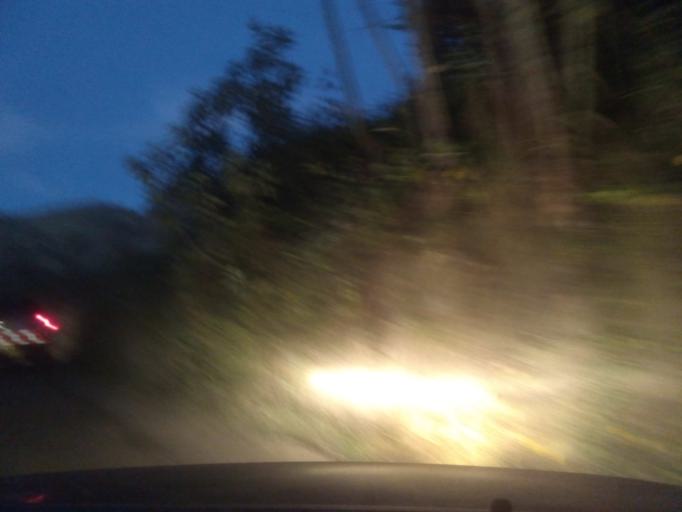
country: PE
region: La Libertad
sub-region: Provincia de Otuzco
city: Mache
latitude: -8.0318
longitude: -78.4492
